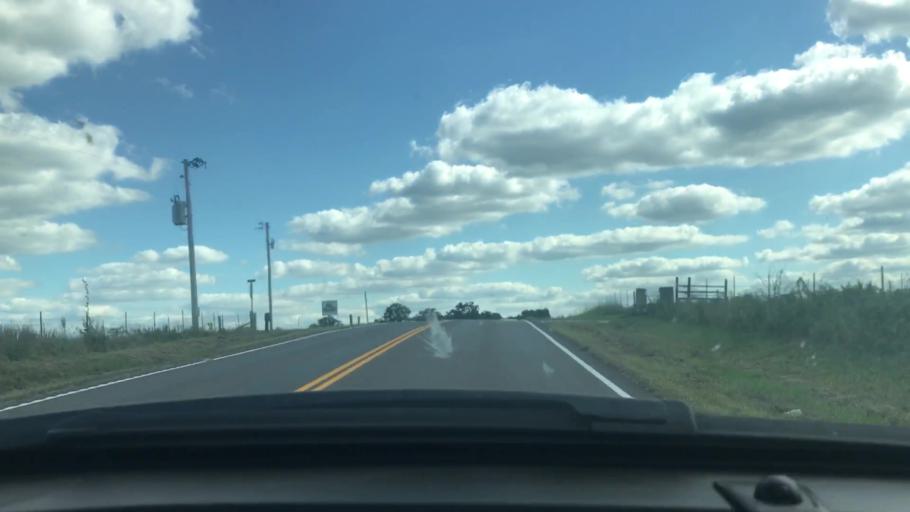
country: US
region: Missouri
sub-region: Wright County
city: Mountain Grove
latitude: 37.2922
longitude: -92.3081
